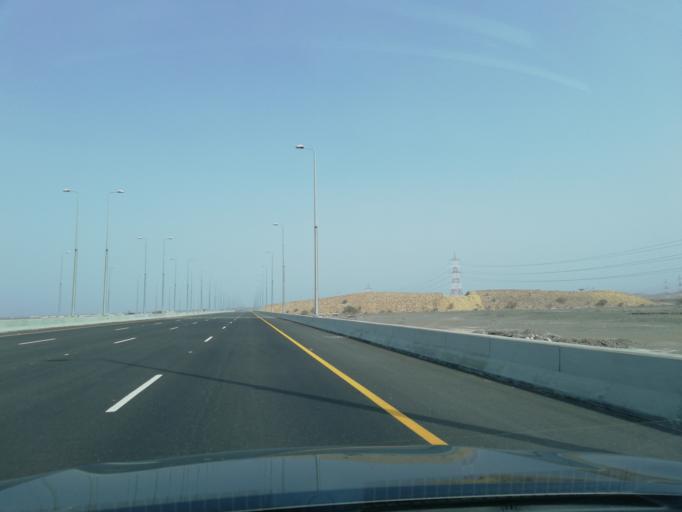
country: OM
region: Al Batinah
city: Al Sohar
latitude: 24.3246
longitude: 56.5675
